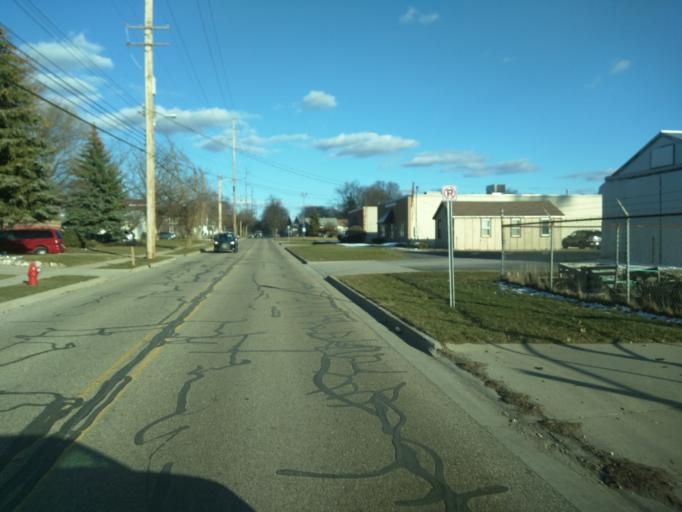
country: US
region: Michigan
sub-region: Ingham County
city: Lansing
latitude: 42.7614
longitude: -84.5607
